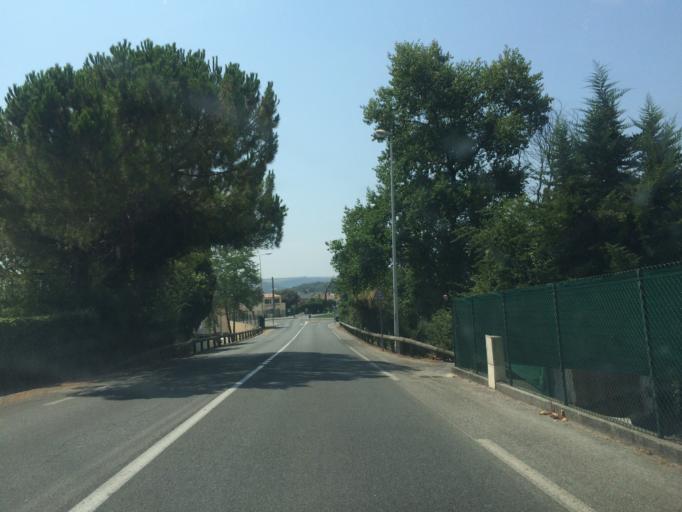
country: FR
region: Provence-Alpes-Cote d'Azur
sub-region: Departement des Alpes-Maritimes
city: La Colle-sur-Loup
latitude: 43.6926
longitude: 7.1058
